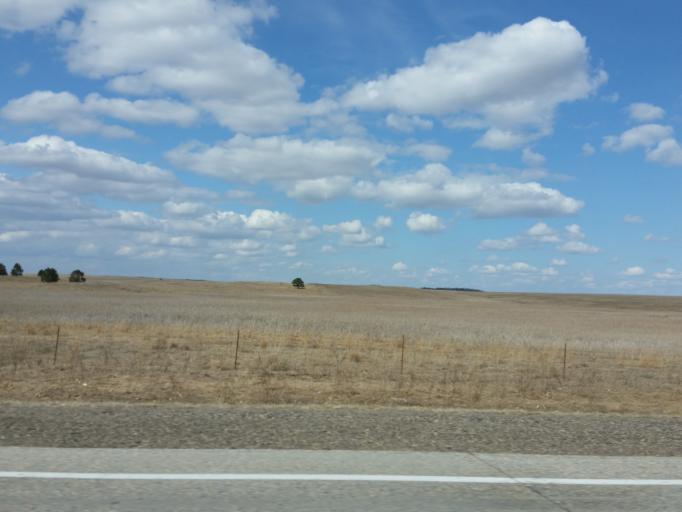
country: US
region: South Dakota
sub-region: Deuel County
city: Clear Lake
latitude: 44.8900
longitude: -96.7662
